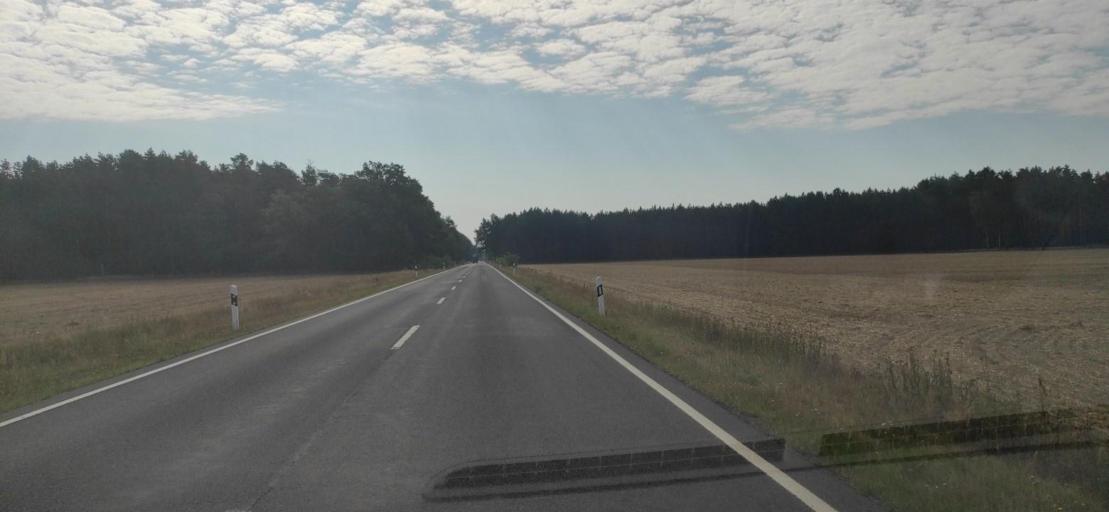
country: DE
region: Brandenburg
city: Forst
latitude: 51.7018
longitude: 14.6925
